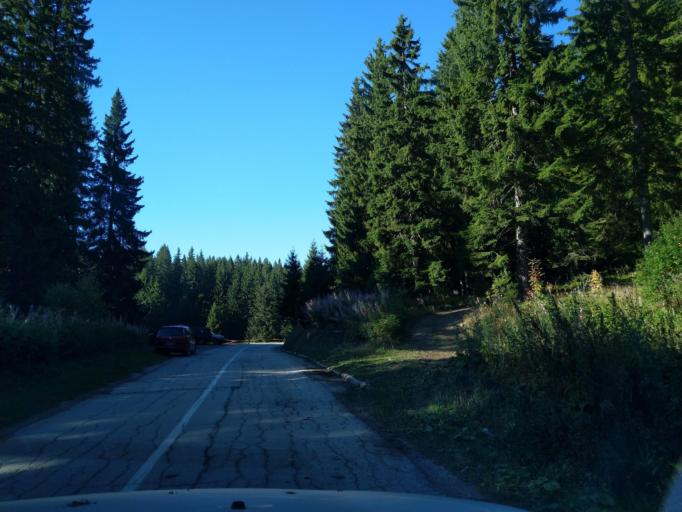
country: RS
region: Central Serbia
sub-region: Moravicki Okrug
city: Ivanjica
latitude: 43.4225
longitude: 20.2640
